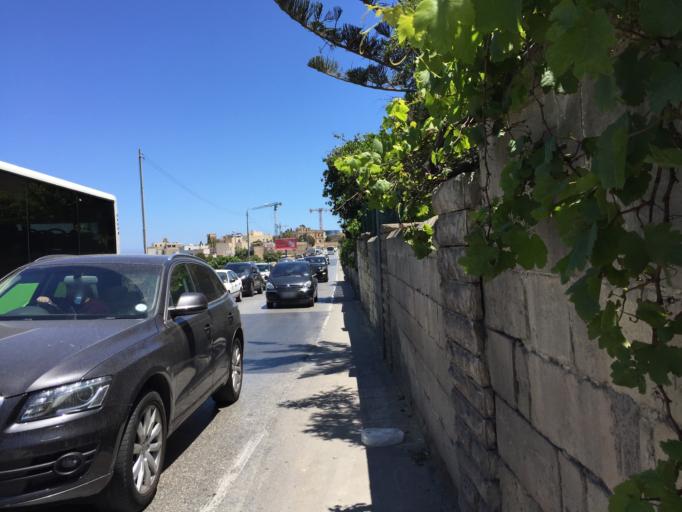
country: MT
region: Is-Swieqi
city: Swieqi
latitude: 35.9232
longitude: 14.4815
